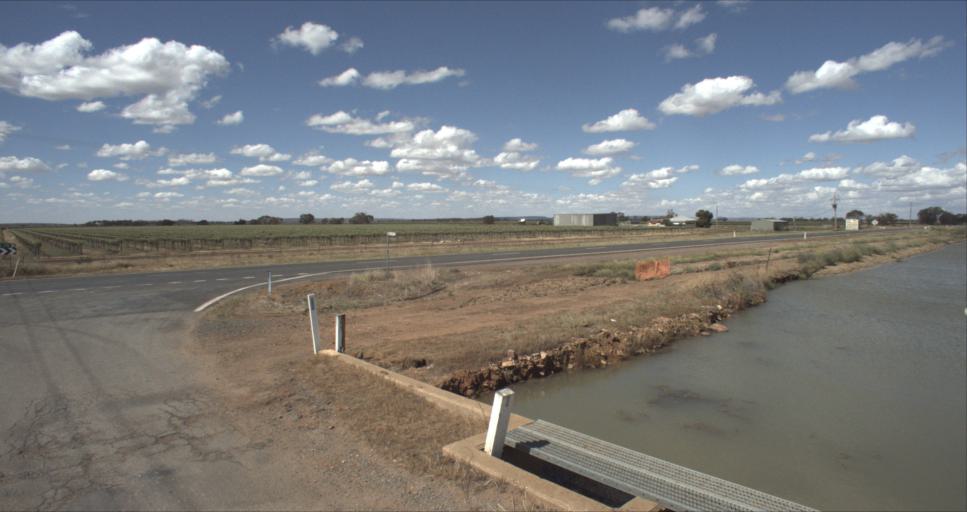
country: AU
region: New South Wales
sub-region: Leeton
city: Leeton
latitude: -34.5086
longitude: 146.2546
